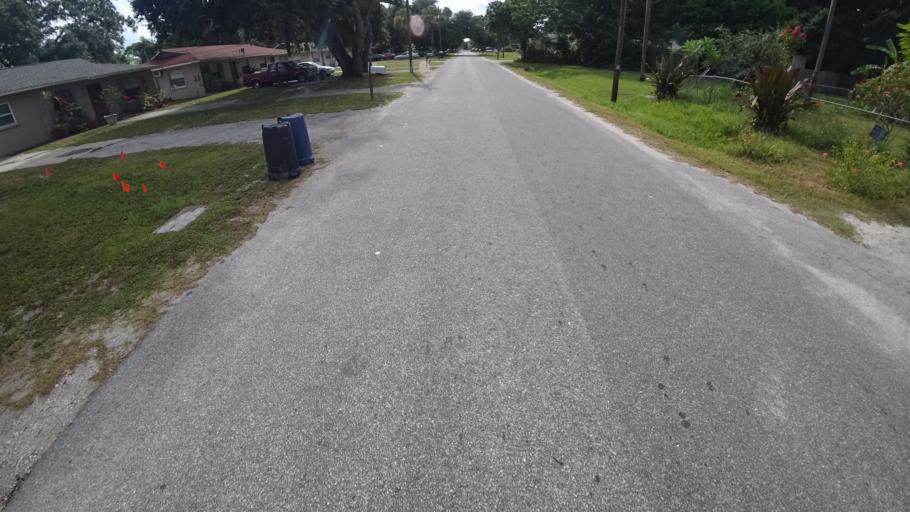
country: US
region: Florida
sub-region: Manatee County
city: Whitfield
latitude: 27.4170
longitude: -82.5496
